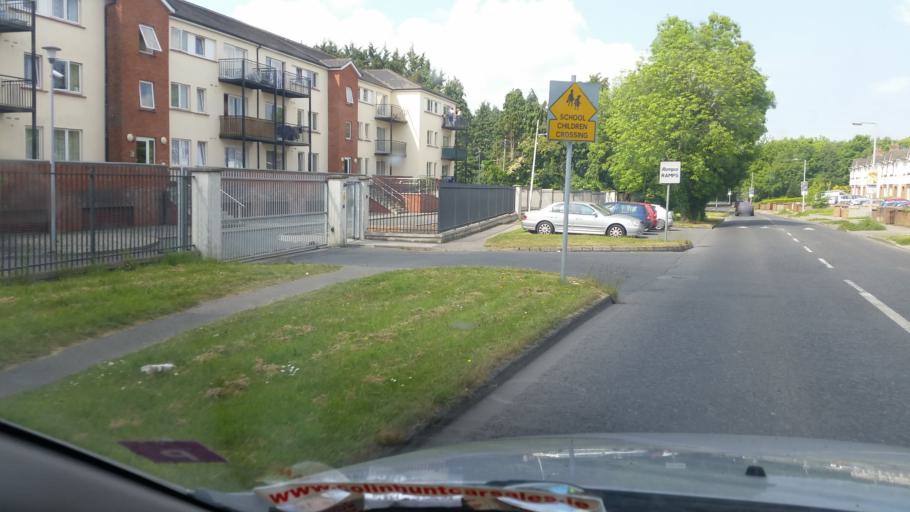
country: IE
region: Leinster
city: Hartstown
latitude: 53.3999
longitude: -6.4009
